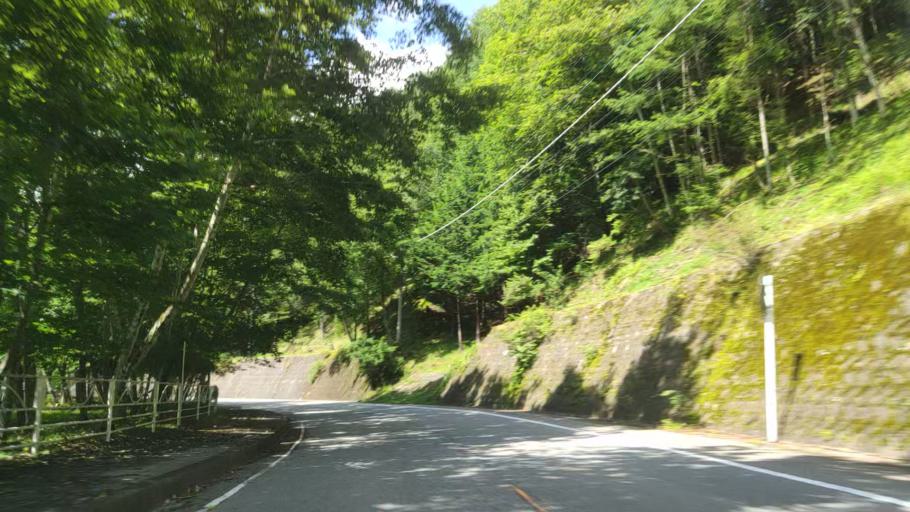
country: JP
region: Yamanashi
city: Enzan
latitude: 35.8533
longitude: 138.7585
